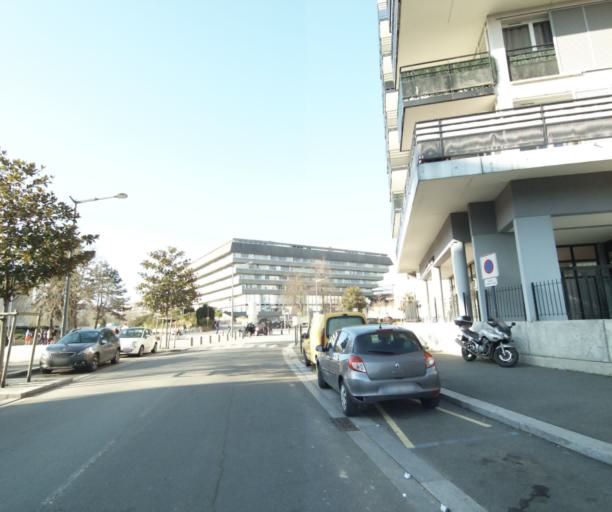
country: FR
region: Ile-de-France
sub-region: Departement du Val-d'Oise
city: Cergy
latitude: 49.0338
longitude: 2.0785
